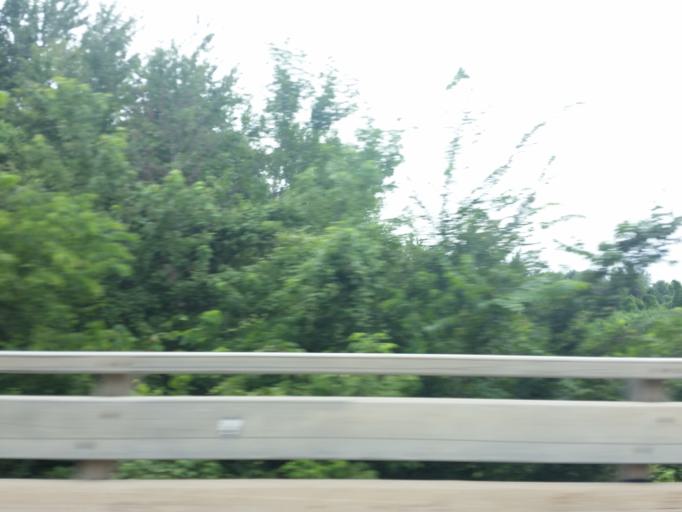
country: US
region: Illinois
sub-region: Alexander County
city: Cairo
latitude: 36.9730
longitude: -89.1459
